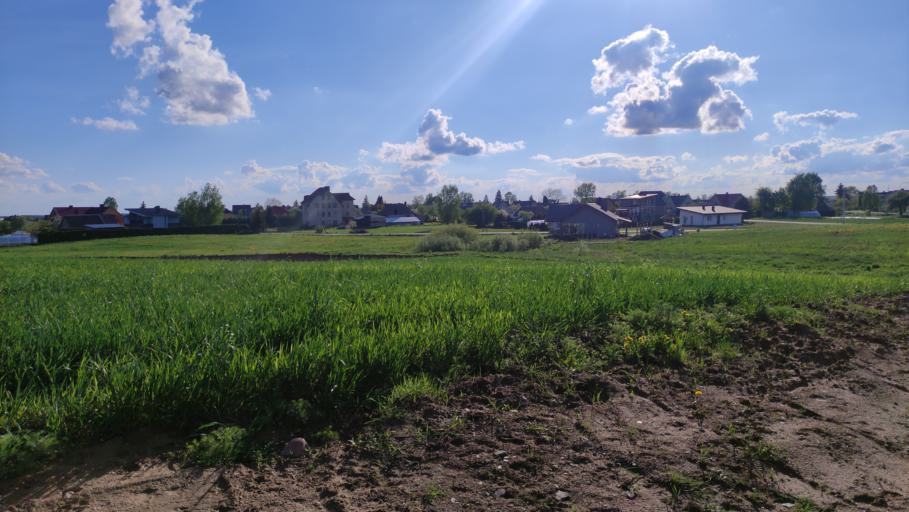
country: LT
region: Alytaus apskritis
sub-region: Alytus
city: Alytus
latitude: 54.4361
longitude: 24.0029
